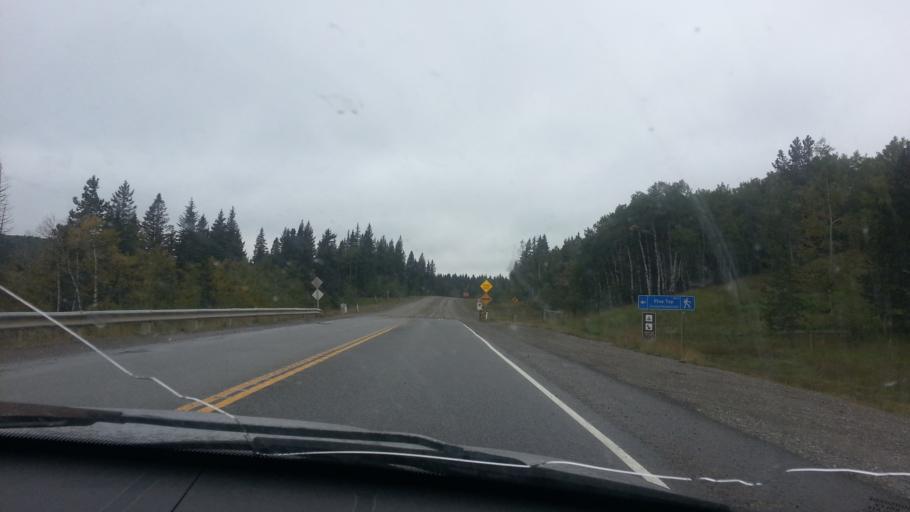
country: CA
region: Alberta
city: Cochrane
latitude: 51.0370
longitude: -114.7242
